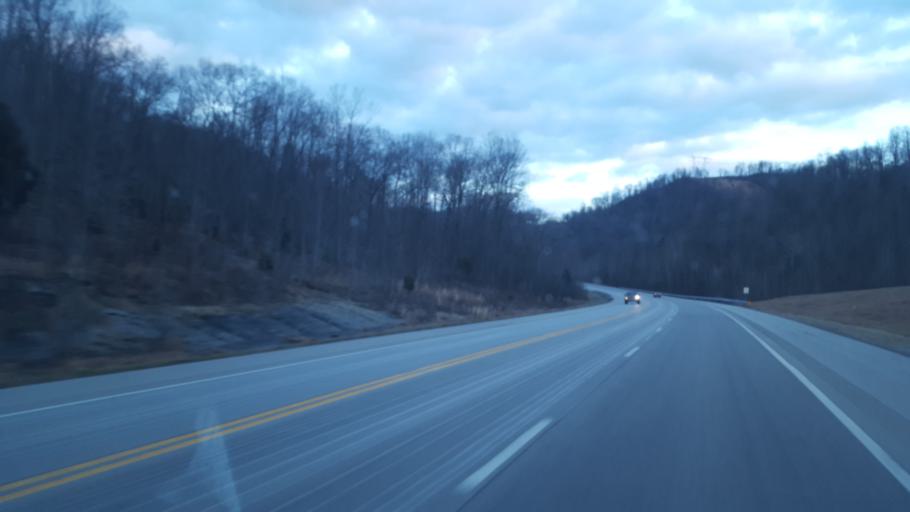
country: US
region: Kentucky
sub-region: Lewis County
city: Vanceburg
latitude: 38.5769
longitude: -83.3219
